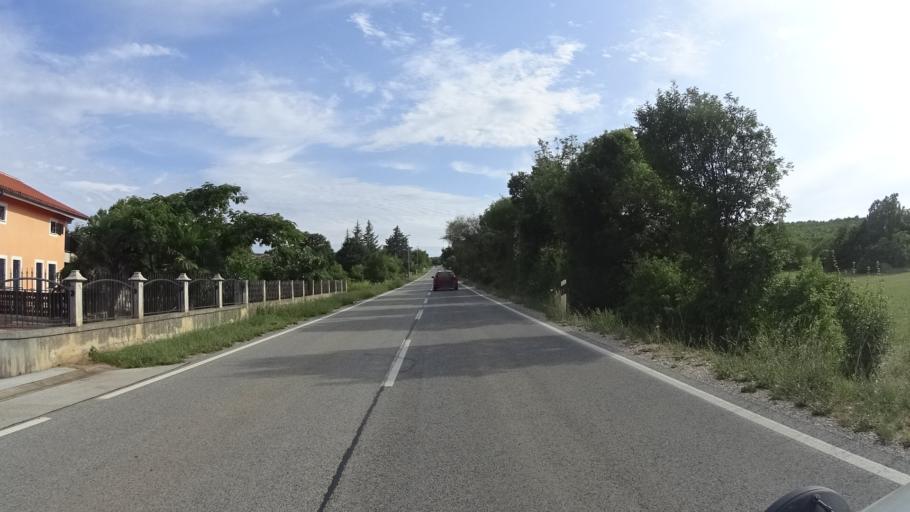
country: HR
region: Istarska
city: Rasa
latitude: 45.0699
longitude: 14.0930
